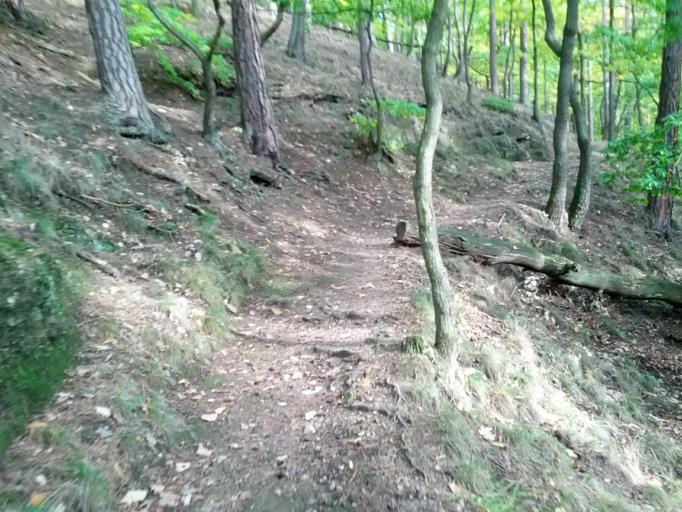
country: DE
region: Thuringia
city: Eisenach
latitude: 50.9644
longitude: 10.3255
